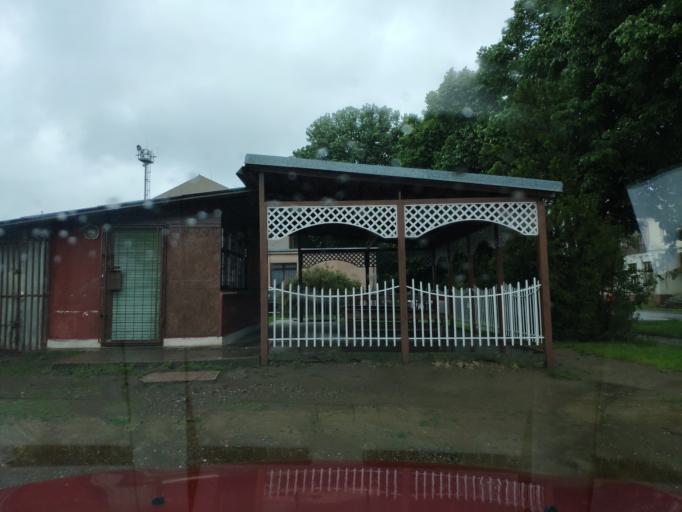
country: SK
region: Kosicky
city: Cierna nad Tisou
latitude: 48.4191
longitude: 22.0861
